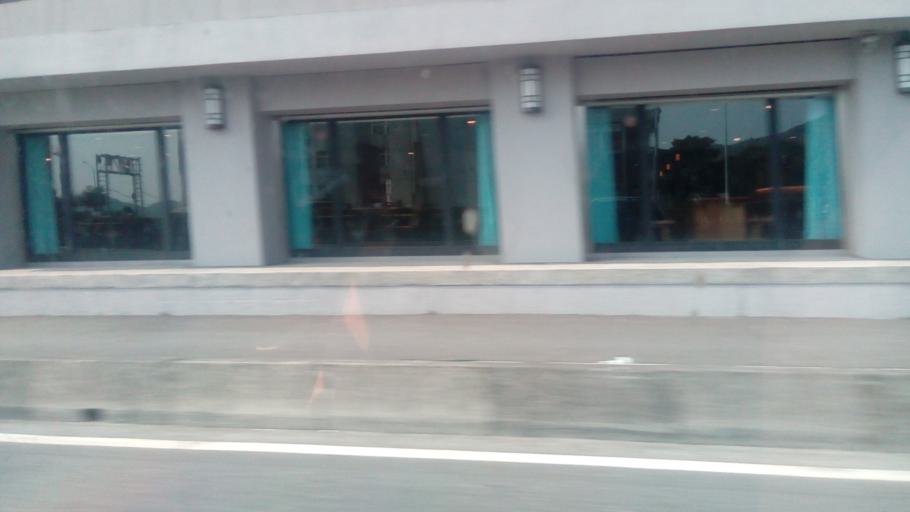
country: TW
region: Taiwan
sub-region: Yilan
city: Yilan
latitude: 24.5962
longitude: 121.8571
